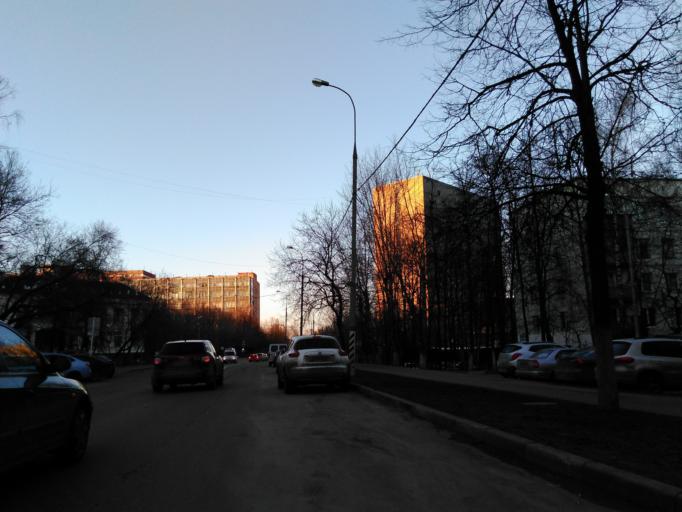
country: RU
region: Moskovskaya
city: Cheremushki
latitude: 55.6446
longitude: 37.5431
